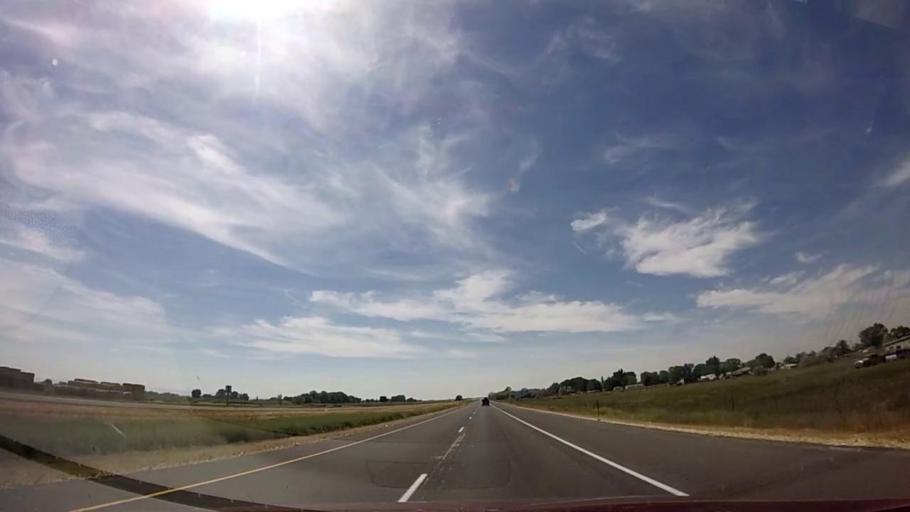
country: US
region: Idaho
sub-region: Minidoka County
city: Rupert
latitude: 42.5690
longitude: -113.6881
